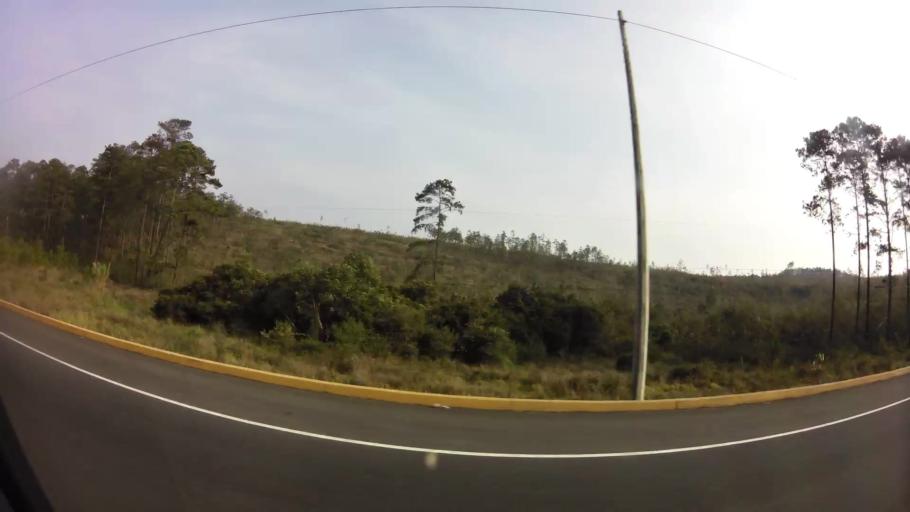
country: HN
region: Francisco Morazan
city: Zambrano
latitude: 14.2890
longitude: -87.4435
